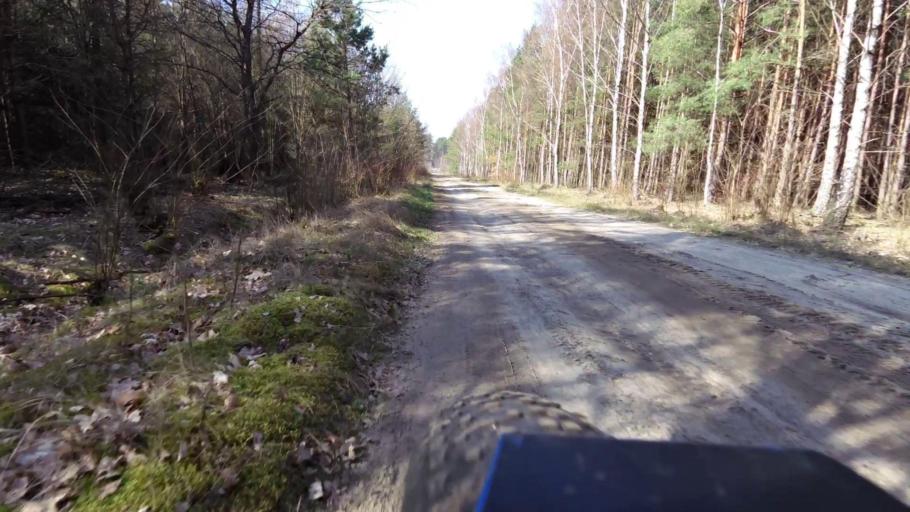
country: PL
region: Lubusz
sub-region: Powiat slubicki
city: Cybinka
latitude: 52.2088
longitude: 14.8659
